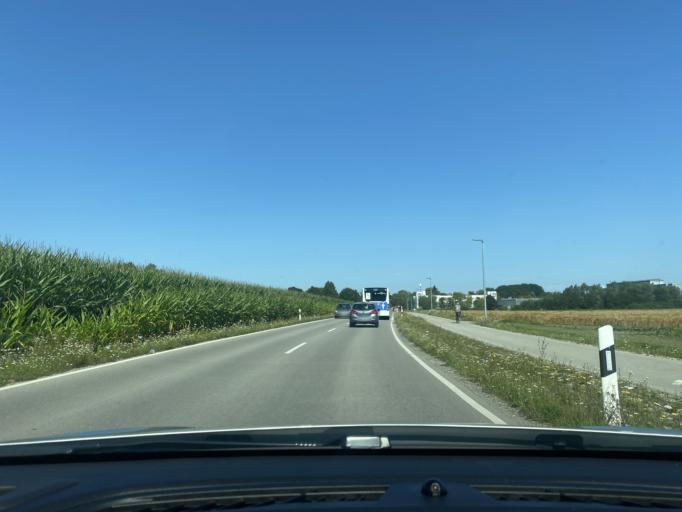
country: DE
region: Bavaria
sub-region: Upper Bavaria
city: Worth
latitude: 48.2721
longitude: 11.9009
